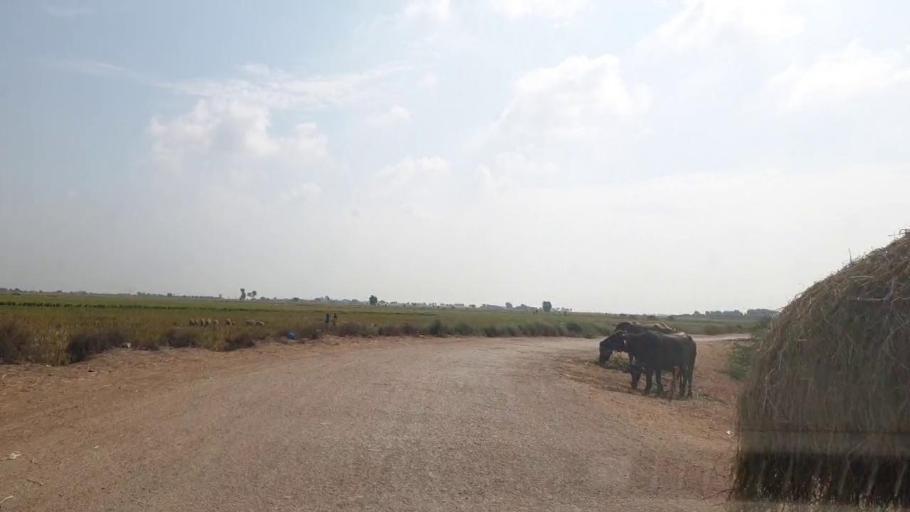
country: PK
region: Sindh
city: Kario
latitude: 24.6422
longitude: 68.5447
